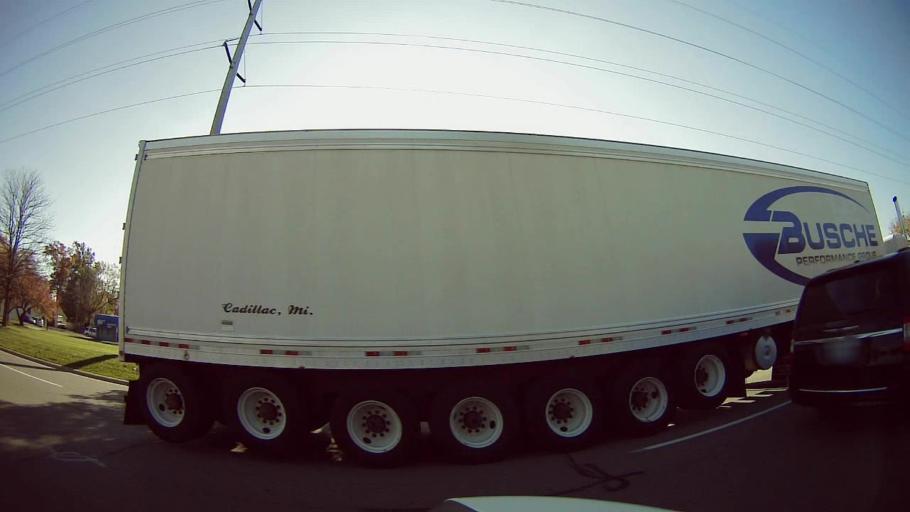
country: US
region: Michigan
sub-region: Oakland County
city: Farmington
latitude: 42.4461
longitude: -83.3306
